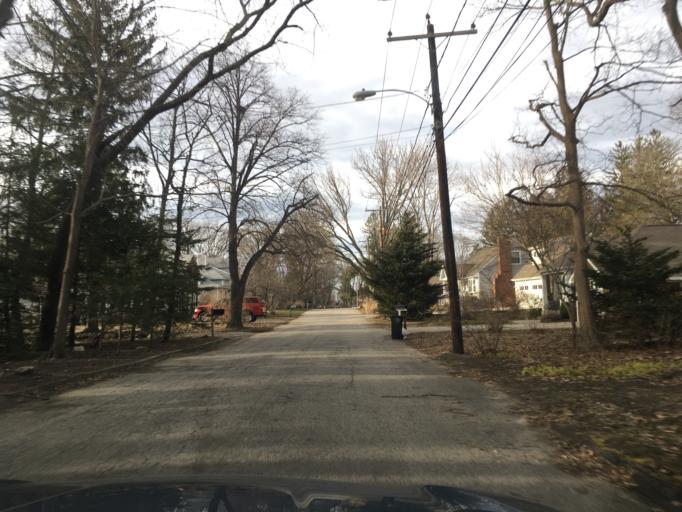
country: US
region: Rhode Island
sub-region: Kent County
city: East Greenwich
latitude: 41.6622
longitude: -71.4189
